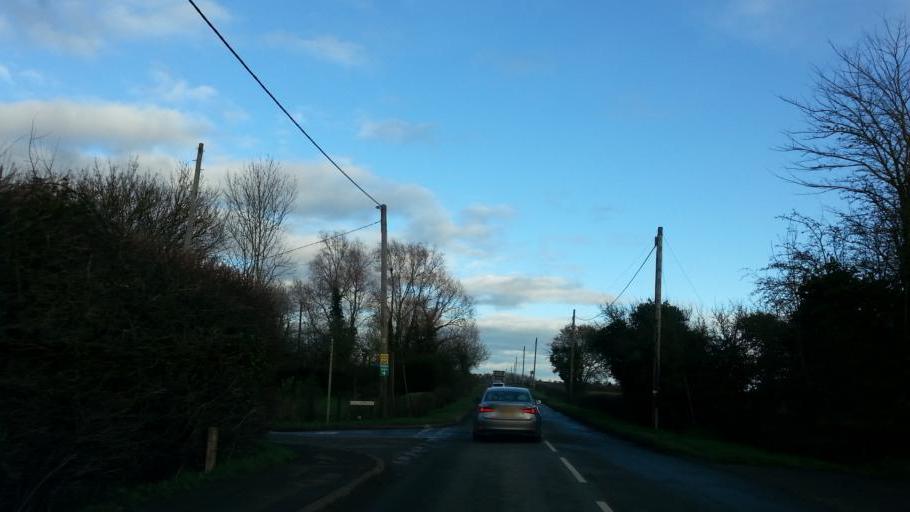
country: GB
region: England
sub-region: Oxfordshire
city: Faringdon
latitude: 51.6160
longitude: -1.6021
